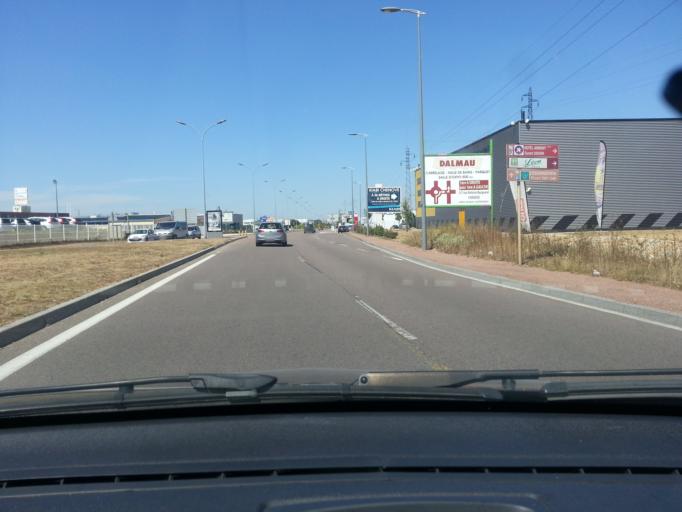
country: FR
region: Bourgogne
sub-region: Departement de la Cote-d'Or
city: Chenove
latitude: 47.2828
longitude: 5.0175
